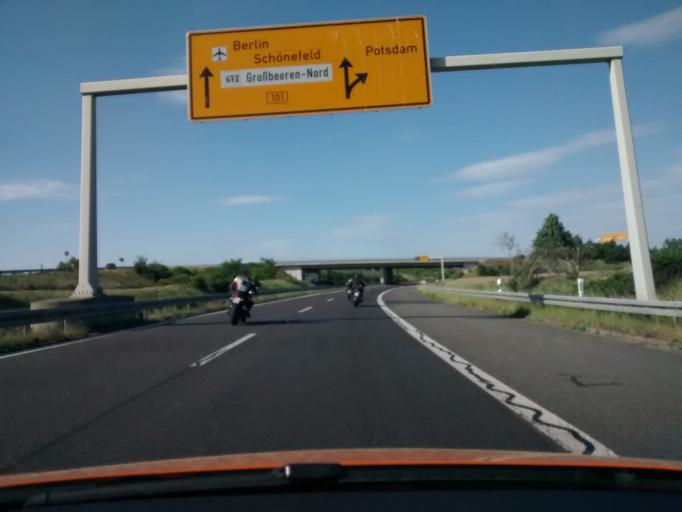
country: DE
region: Brandenburg
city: Grossbeeren
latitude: 52.3470
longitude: 13.2847
